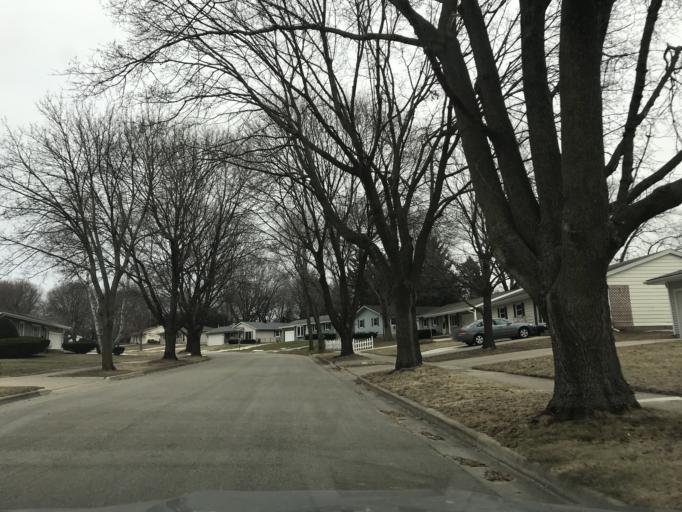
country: US
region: Wisconsin
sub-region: Dane County
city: Monona
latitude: 43.0900
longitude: -89.3037
